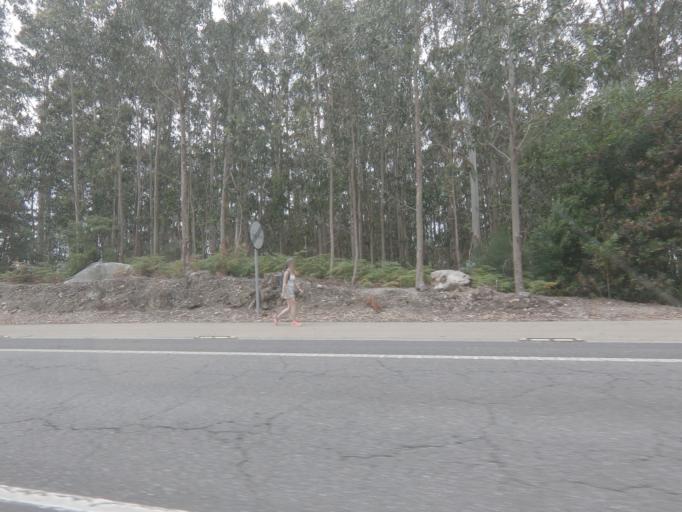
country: ES
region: Galicia
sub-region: Provincia de Pontevedra
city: Oia
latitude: 41.9912
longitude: -8.8814
